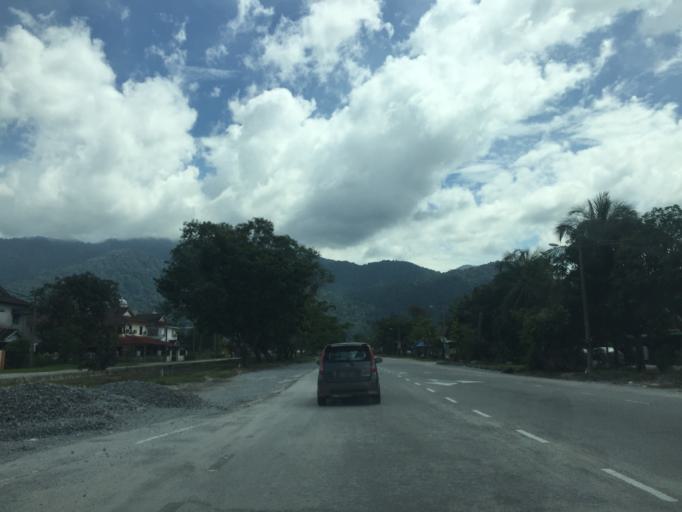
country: MY
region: Perak
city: Kampar
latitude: 4.3266
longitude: 101.1402
